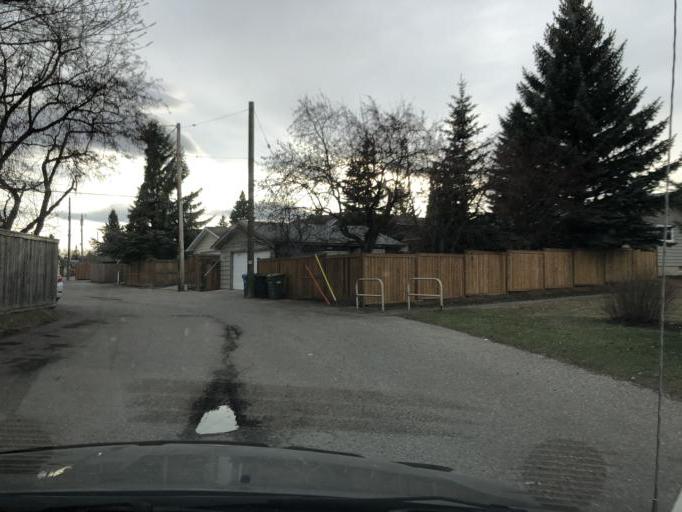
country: CA
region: Alberta
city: Calgary
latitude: 50.9335
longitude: -114.0348
